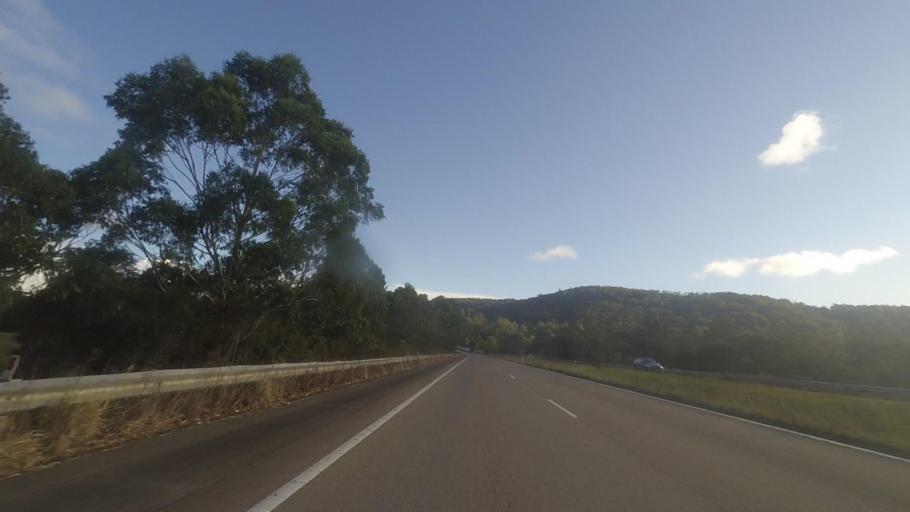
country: AU
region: New South Wales
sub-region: Great Lakes
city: Nabiac
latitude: -32.2705
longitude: 152.3285
